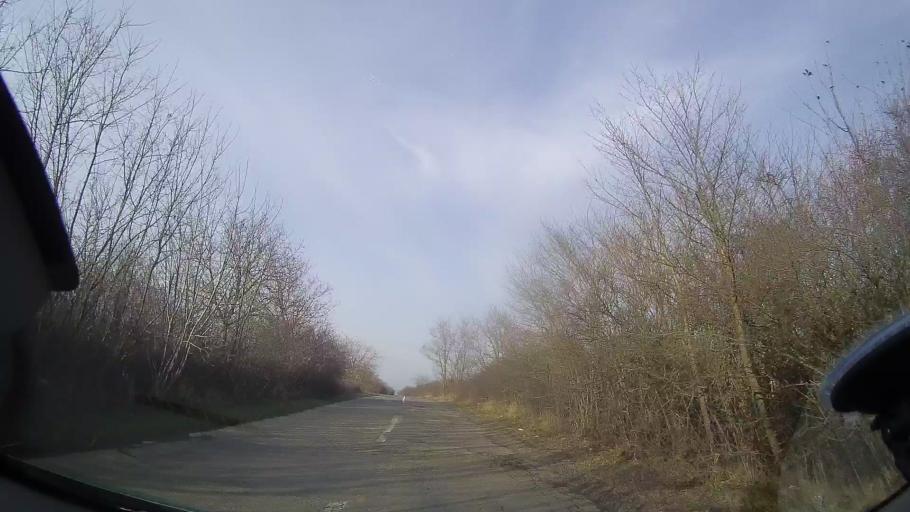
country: RO
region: Bihor
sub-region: Comuna Spinus
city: Spinus
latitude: 47.2126
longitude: 22.1779
